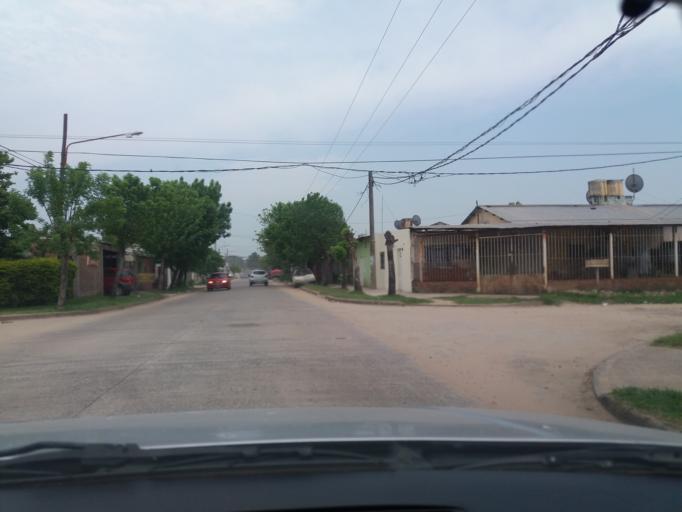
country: AR
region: Corrientes
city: Corrientes
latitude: -27.5114
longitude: -58.8001
